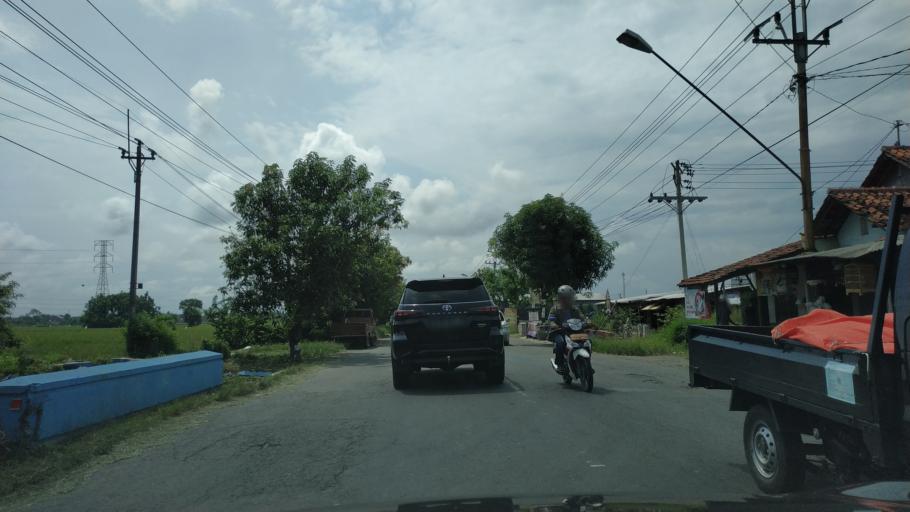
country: ID
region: Central Java
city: Adiwerna
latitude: -6.9190
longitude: 109.1262
